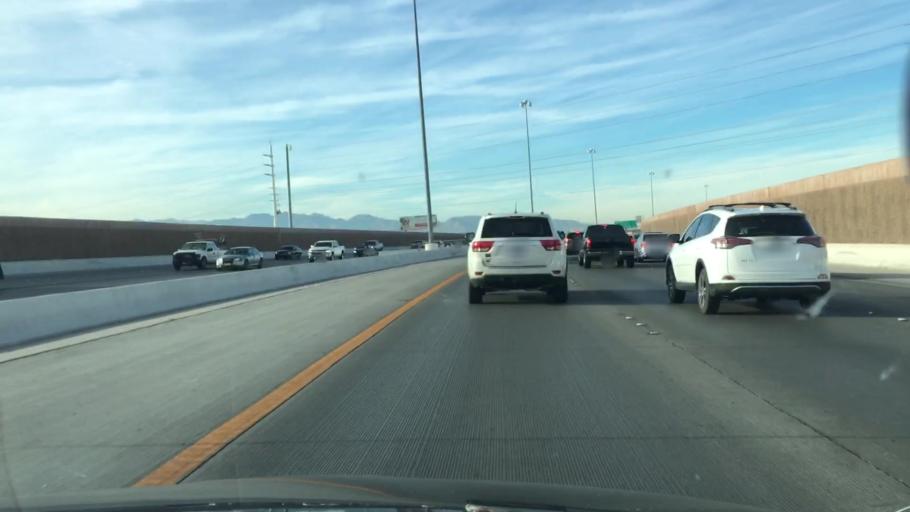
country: US
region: Nevada
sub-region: Clark County
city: Whitney
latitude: 36.0271
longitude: -115.1290
